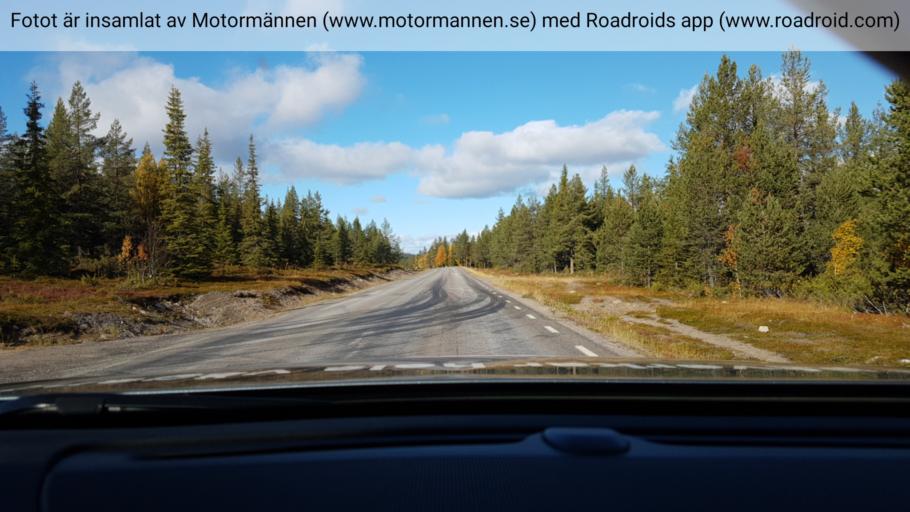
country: SE
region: Norrbotten
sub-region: Arjeplogs Kommun
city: Arjeplog
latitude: 65.9073
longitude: 18.3528
